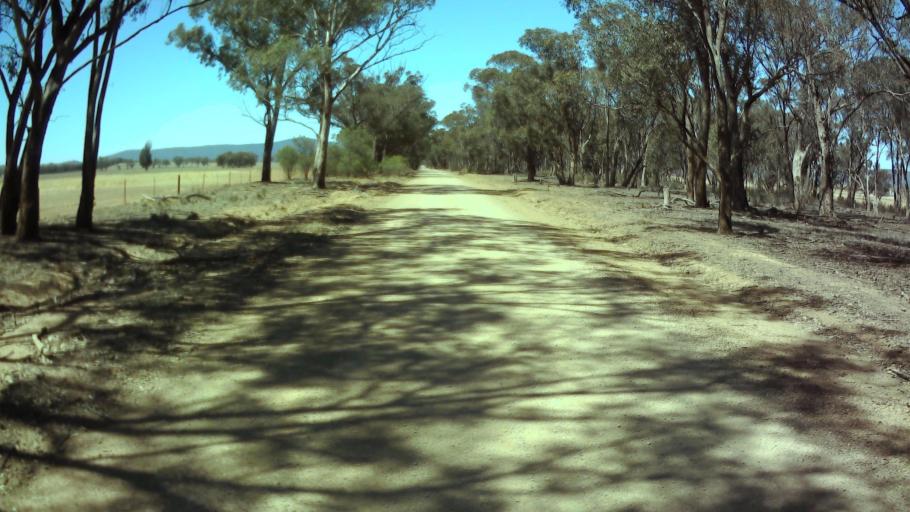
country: AU
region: New South Wales
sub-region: Weddin
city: Grenfell
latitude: -33.8922
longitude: 148.0861
